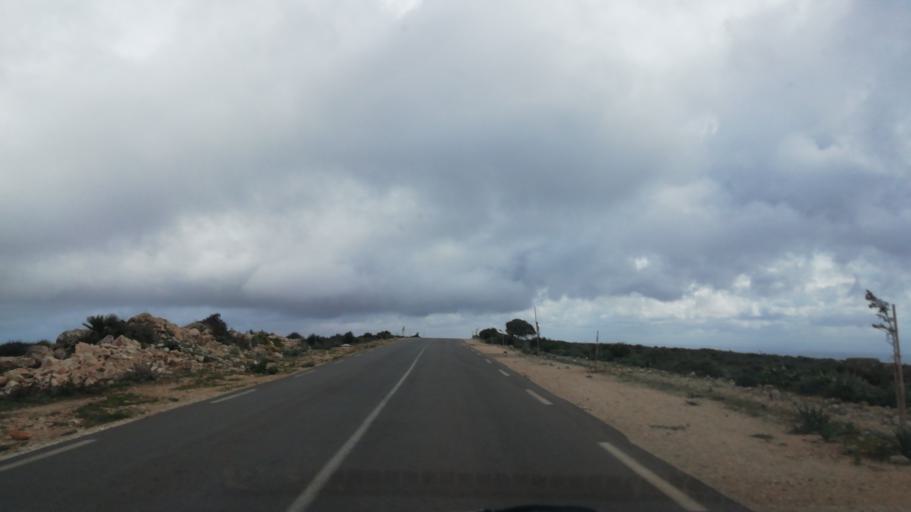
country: DZ
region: Oran
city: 'Ain el Turk
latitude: 35.6995
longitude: -0.7553
